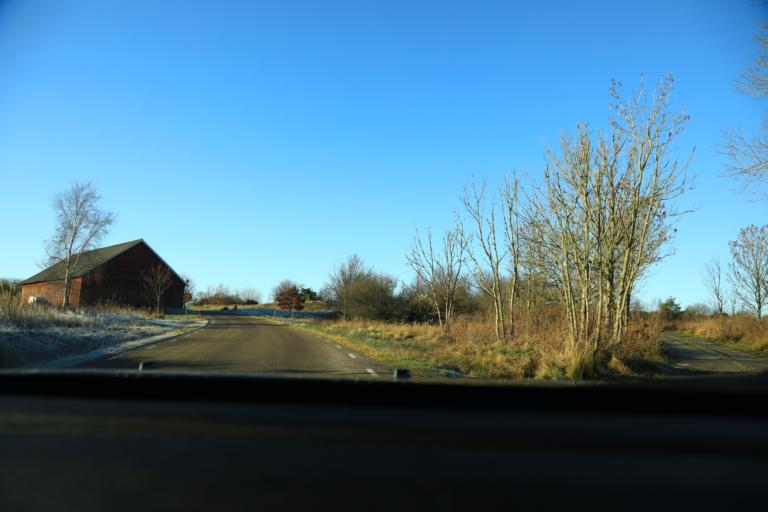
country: SE
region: Halland
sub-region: Varbergs Kommun
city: Varberg
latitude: 57.2057
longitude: 12.2142
